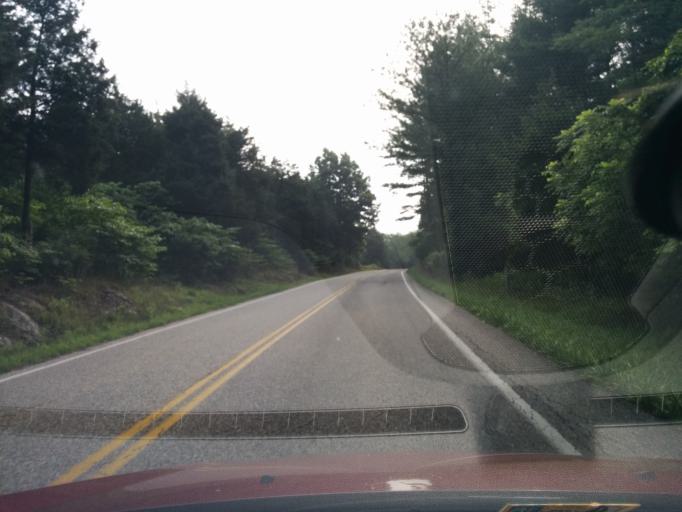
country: US
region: Virginia
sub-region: City of Lexington
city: Lexington
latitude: 37.7457
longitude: -79.5060
